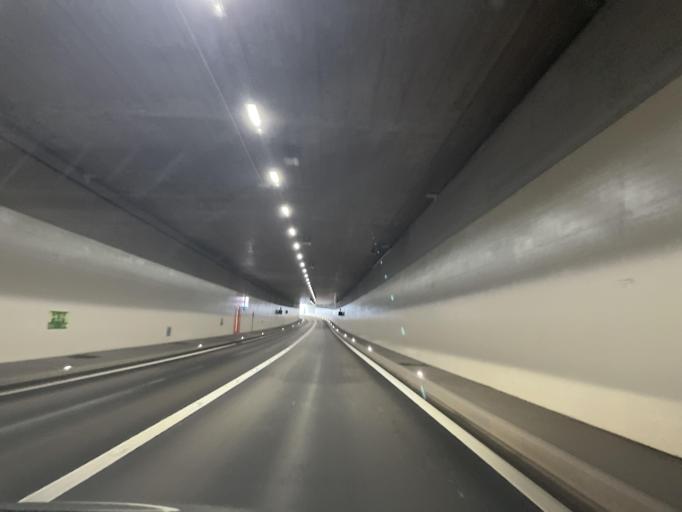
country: CH
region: Saint Gallen
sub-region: Wahlkreis Toggenburg
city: Buetschwil
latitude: 47.3467
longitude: 9.0819
